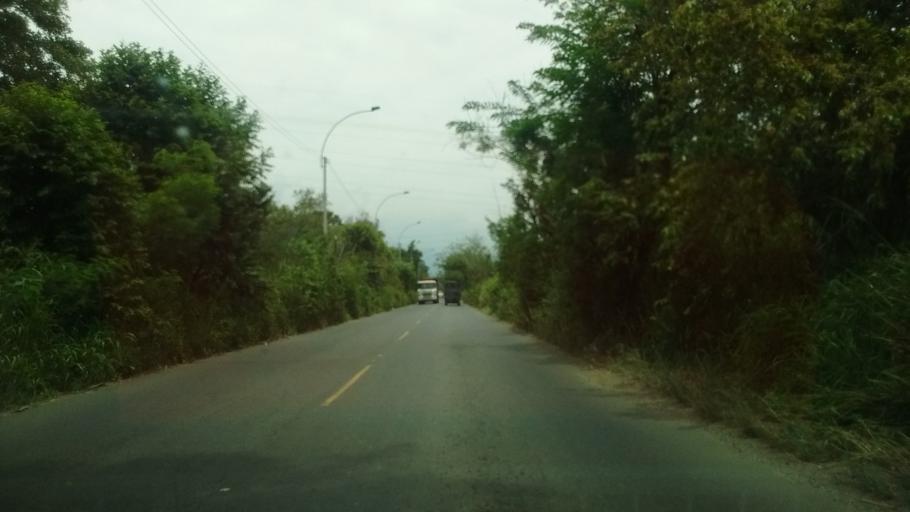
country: CO
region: Valle del Cauca
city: Jamundi
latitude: 3.3330
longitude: -76.5112
